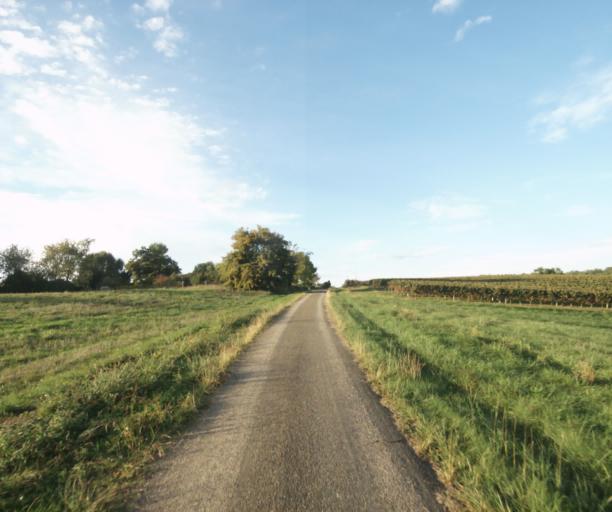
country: FR
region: Midi-Pyrenees
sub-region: Departement du Gers
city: Le Houga
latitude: 43.8374
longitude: -0.1145
